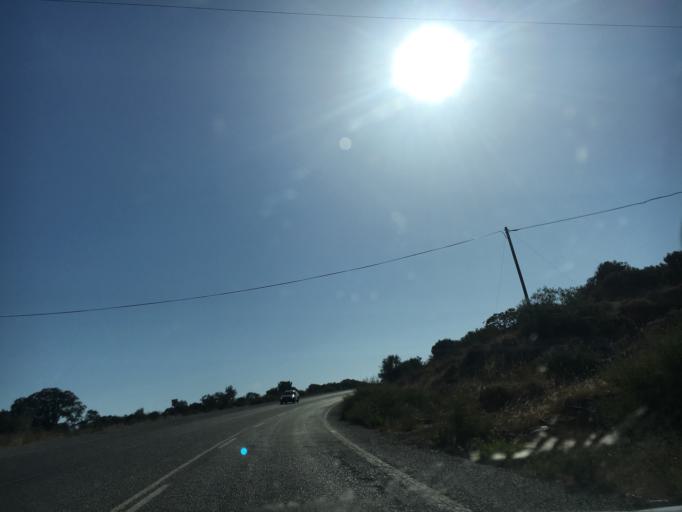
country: TR
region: Canakkale
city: Behram
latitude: 39.5049
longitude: 26.4021
